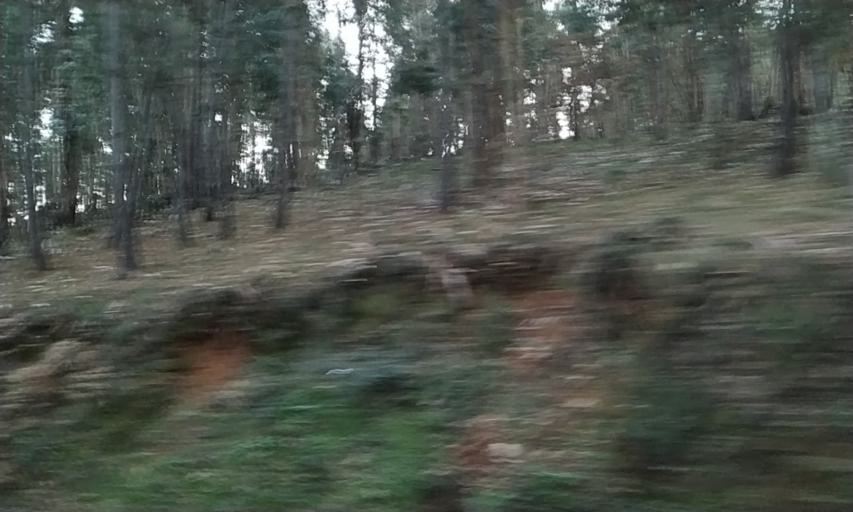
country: PT
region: Vila Real
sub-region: Mondim de Basto
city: Mondim de Basto
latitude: 41.4564
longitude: -7.9600
